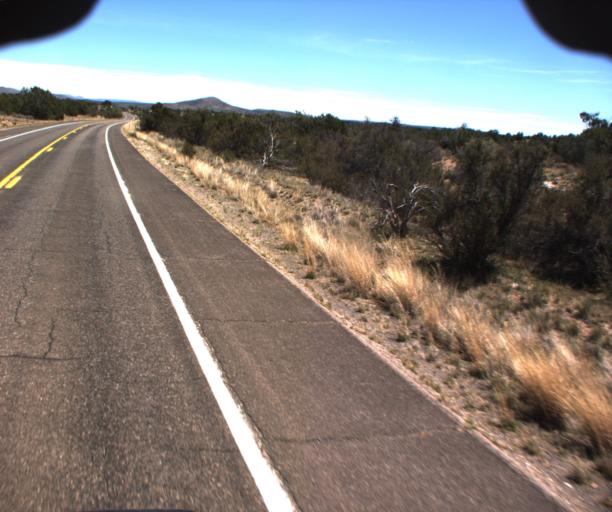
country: US
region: Arizona
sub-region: Mohave County
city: Peach Springs
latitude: 35.5539
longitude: -113.3727
